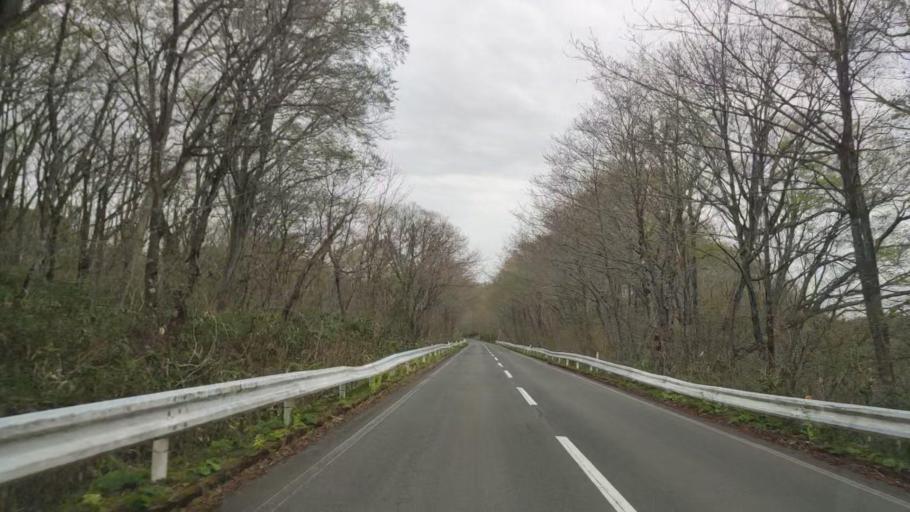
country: JP
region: Akita
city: Hanawa
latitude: 40.4055
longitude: 140.8100
